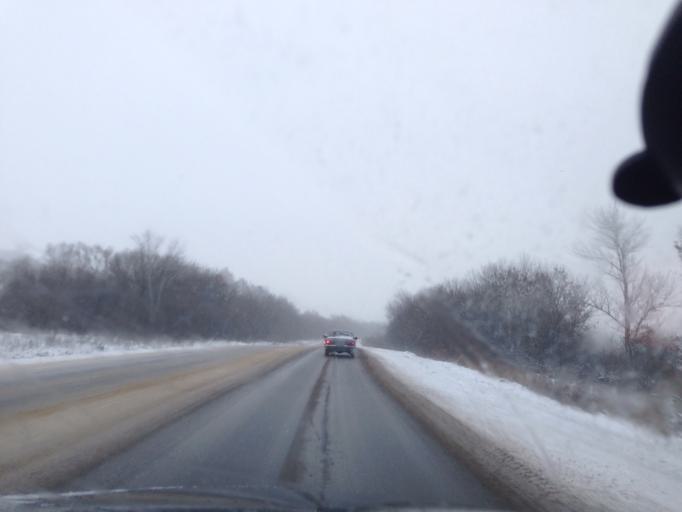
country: RU
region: Tula
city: Bolokhovo
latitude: 54.1059
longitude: 37.7578
